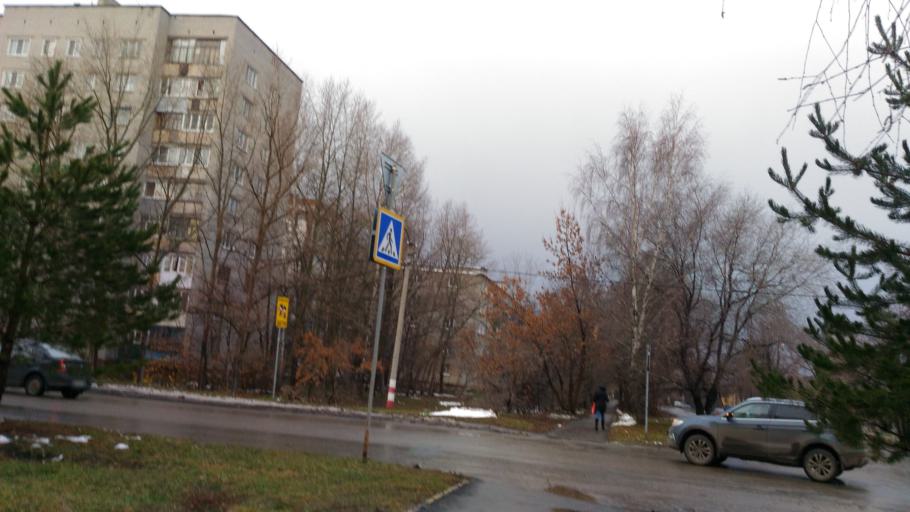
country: RU
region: Ulyanovsk
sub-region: Ulyanovskiy Rayon
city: Ulyanovsk
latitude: 54.3486
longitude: 48.3887
